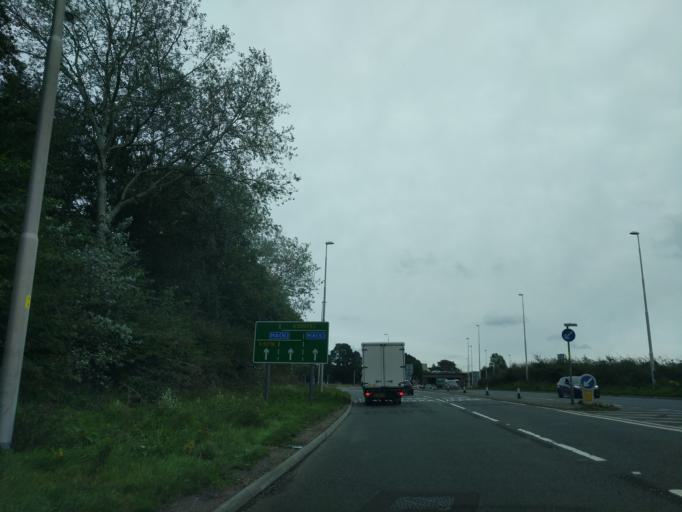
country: GB
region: England
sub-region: Cheshire East
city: Alsager
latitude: 53.0684
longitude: -2.3369
